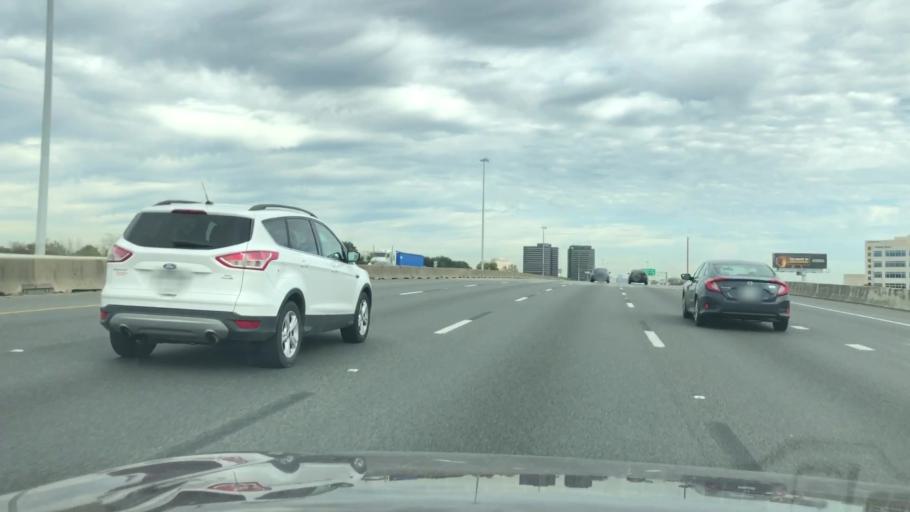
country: US
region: Texas
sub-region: Harris County
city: Piney Point Village
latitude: 29.6913
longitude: -95.5276
